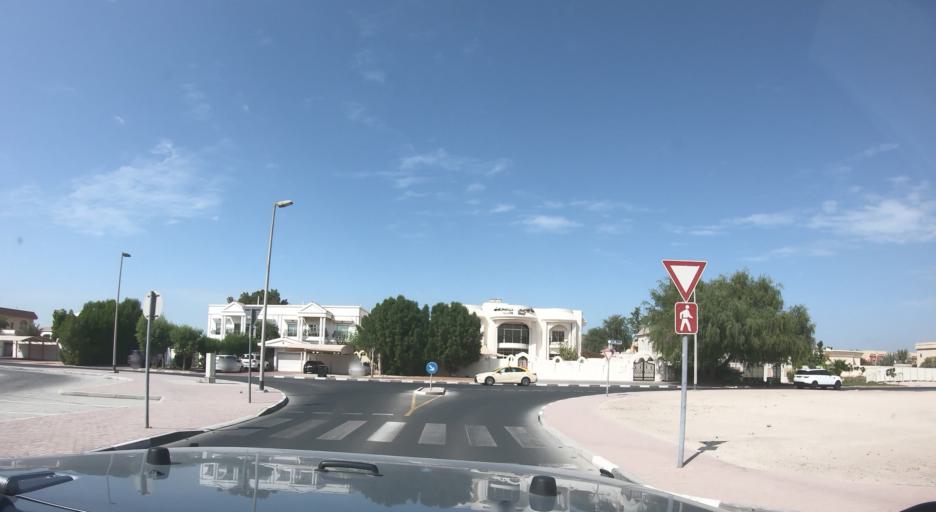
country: AE
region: Dubai
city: Dubai
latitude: 25.1569
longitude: 55.2223
